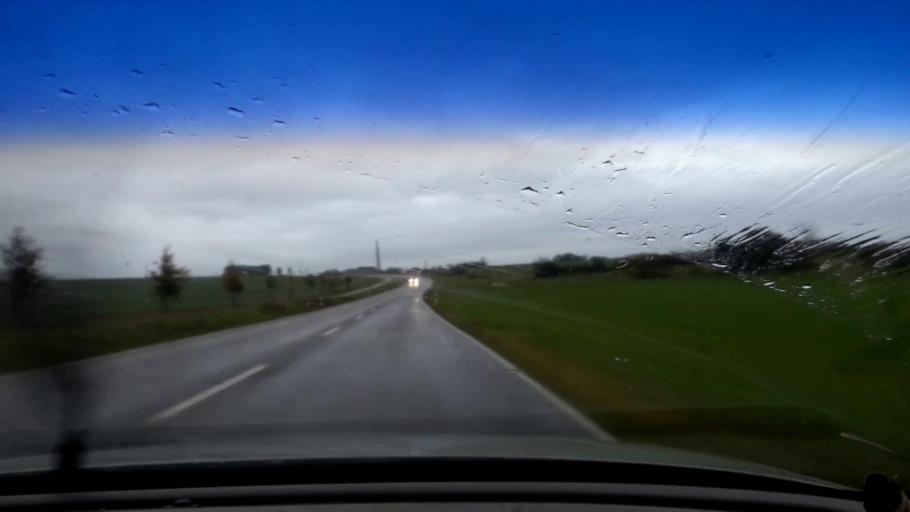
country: DE
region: Bavaria
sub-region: Upper Franconia
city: Walsdorf
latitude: 49.8785
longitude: 10.7828
